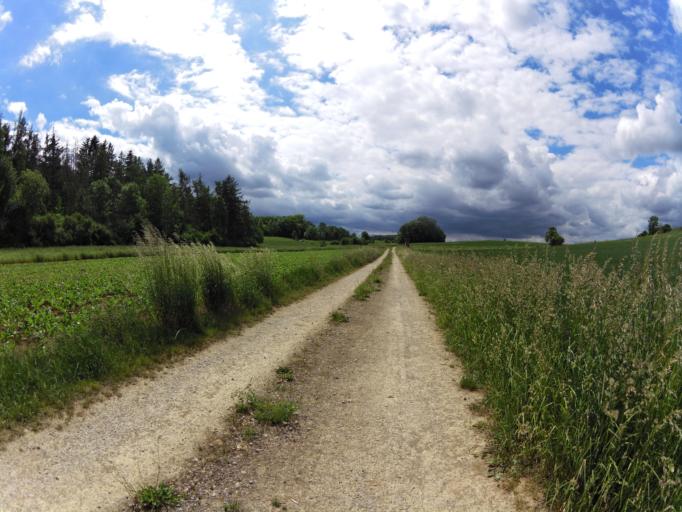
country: DE
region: Bavaria
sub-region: Regierungsbezirk Unterfranken
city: Gaukonigshofen
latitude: 49.6674
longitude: 9.9937
